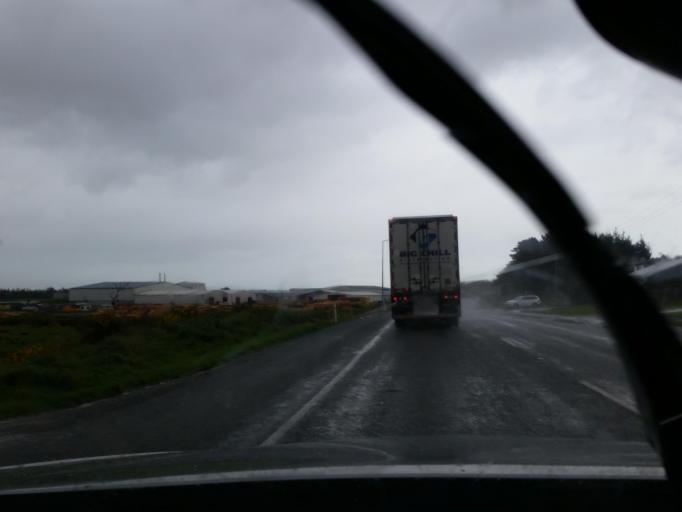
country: NZ
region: Southland
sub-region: Invercargill City
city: Invercargill
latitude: -46.4550
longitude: 168.3644
